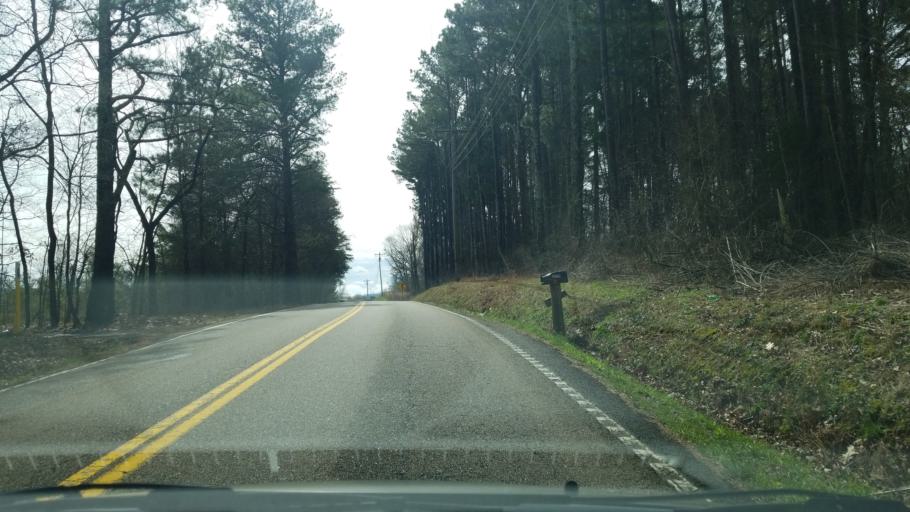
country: US
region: Tennessee
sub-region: Hamilton County
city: Harrison
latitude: 35.1306
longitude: -85.0699
